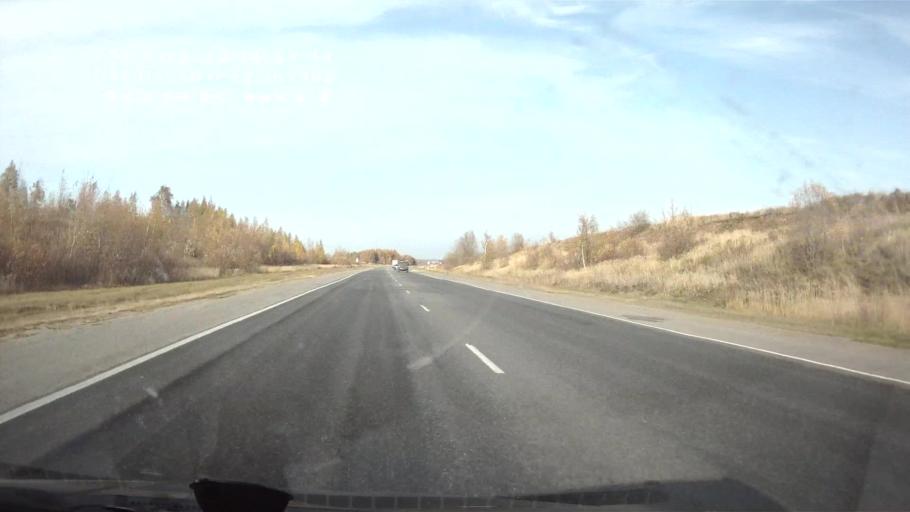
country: RU
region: Chuvashia
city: Kugesi
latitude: 56.0431
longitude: 47.3672
